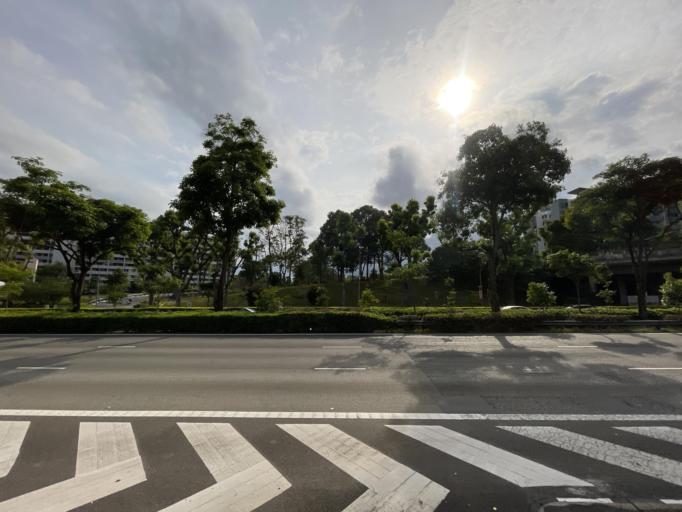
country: SG
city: Singapore
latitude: 1.3141
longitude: 103.7610
